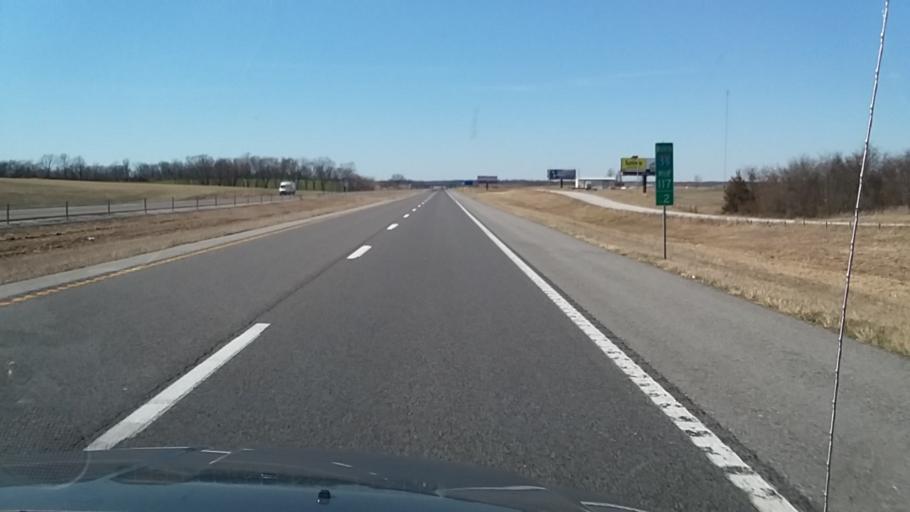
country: US
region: Missouri
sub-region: Perry County
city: Perryville
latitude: 37.5680
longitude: -89.7506
